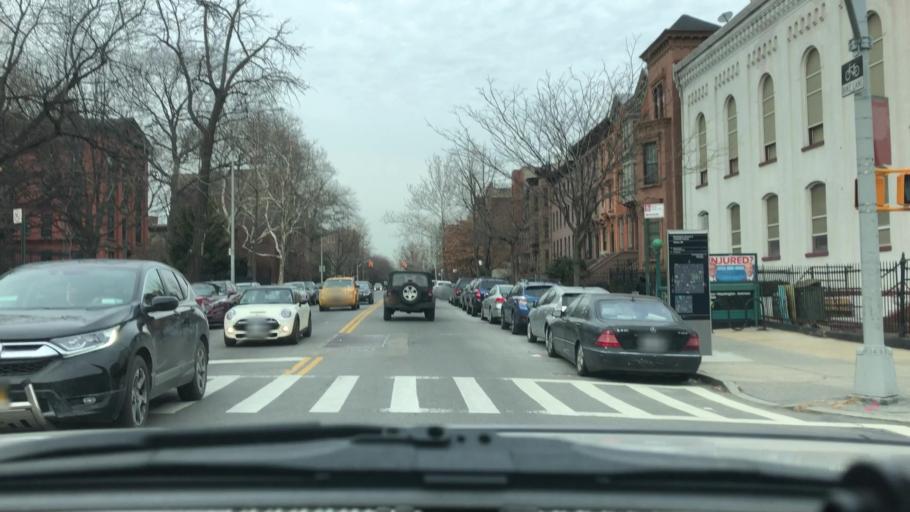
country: US
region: New York
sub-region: Kings County
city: Brooklyn
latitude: 40.6882
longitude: -73.9658
